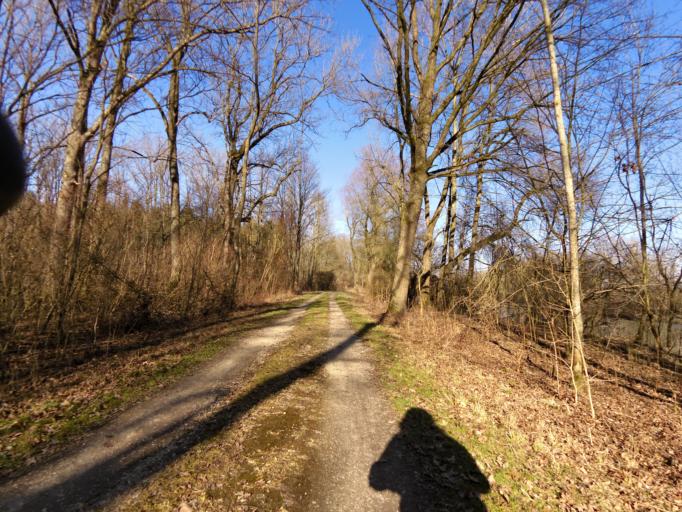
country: DE
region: Bavaria
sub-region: Lower Bavaria
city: Eching
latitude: 48.5103
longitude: 12.0740
